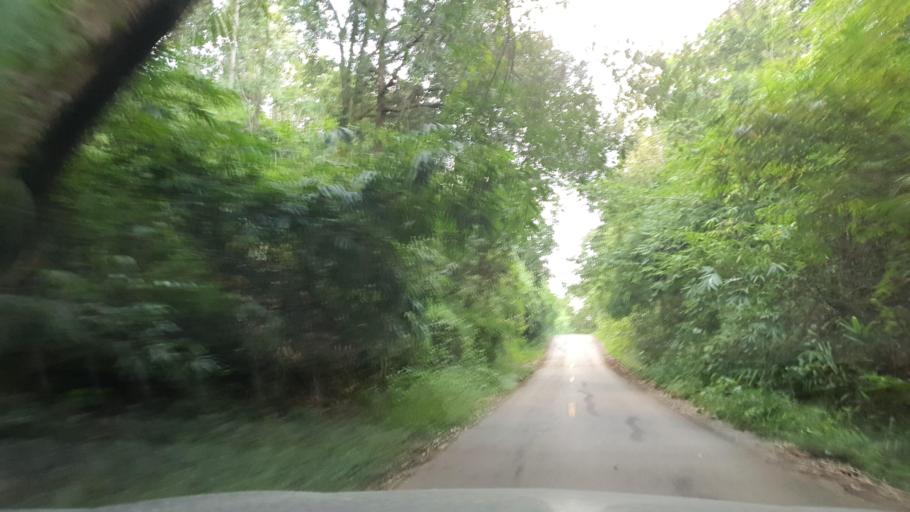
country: TH
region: Chiang Mai
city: Mae On
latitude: 18.8748
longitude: 99.2596
